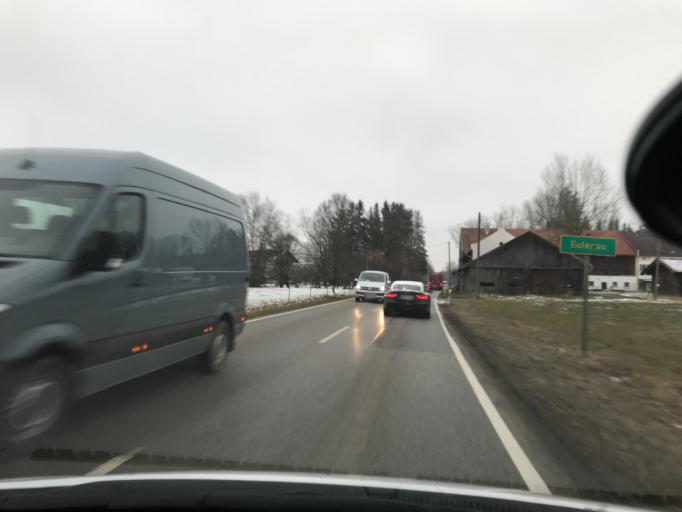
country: DE
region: Bavaria
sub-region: Upper Bavaria
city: Bad Feilnbach
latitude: 47.8144
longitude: 12.0154
